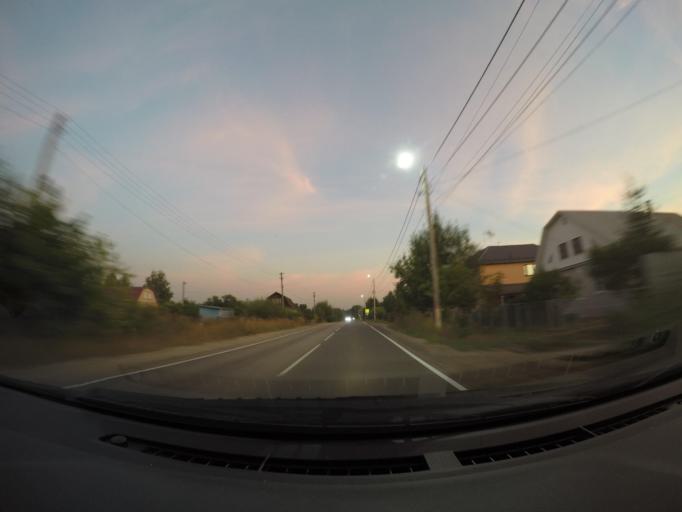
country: RU
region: Moskovskaya
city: Gzhel'
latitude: 55.5766
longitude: 38.3959
